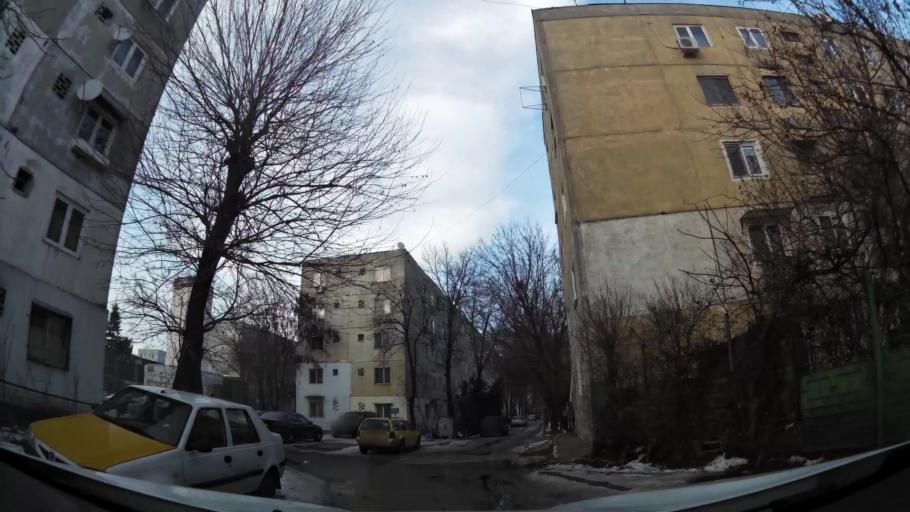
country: RO
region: Bucuresti
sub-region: Municipiul Bucuresti
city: Bucuresti
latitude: 44.3917
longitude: 26.0782
